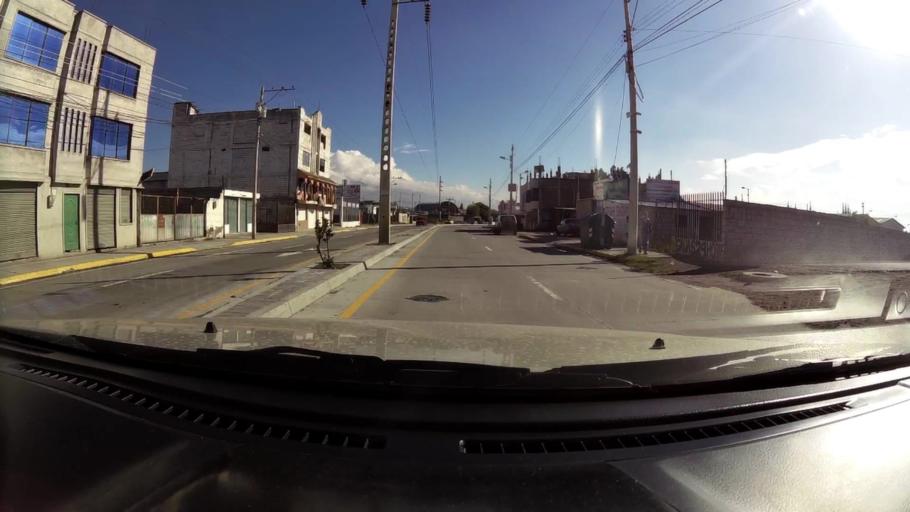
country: EC
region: Chimborazo
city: Riobamba
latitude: -1.6488
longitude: -78.6891
